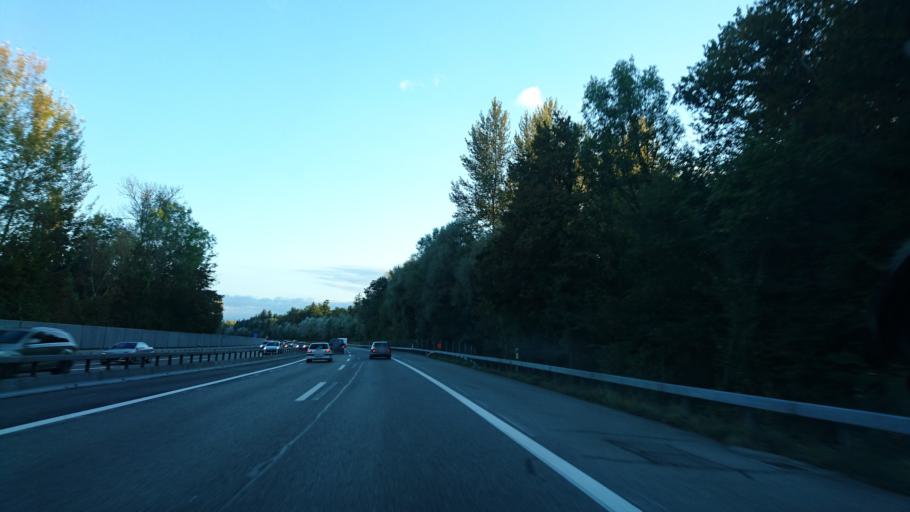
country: CH
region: Bern
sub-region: Bern-Mittelland District
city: Rubigen
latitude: 46.8970
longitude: 7.5335
